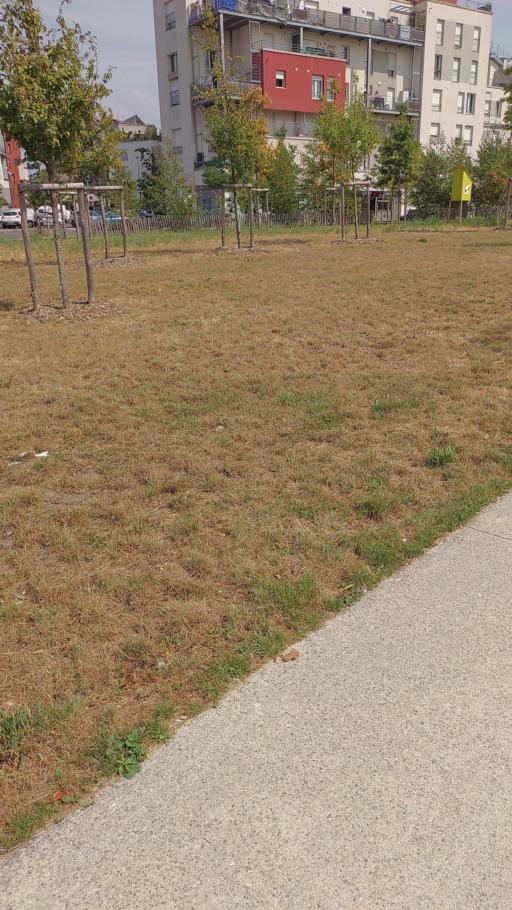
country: FR
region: Ile-de-France
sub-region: Departement du Val-de-Marne
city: Valenton
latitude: 48.7522
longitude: 2.4722
